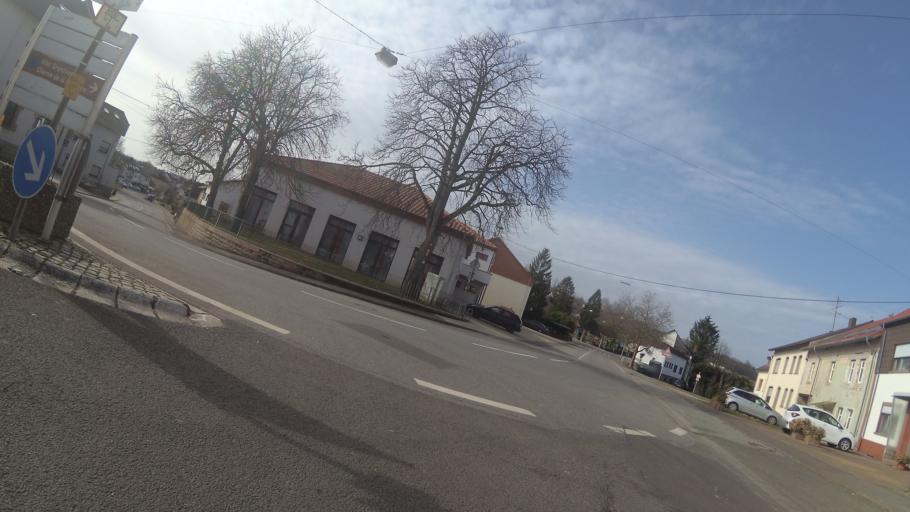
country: DE
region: Saarland
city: Uberherrn
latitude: 49.2644
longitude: 6.6946
